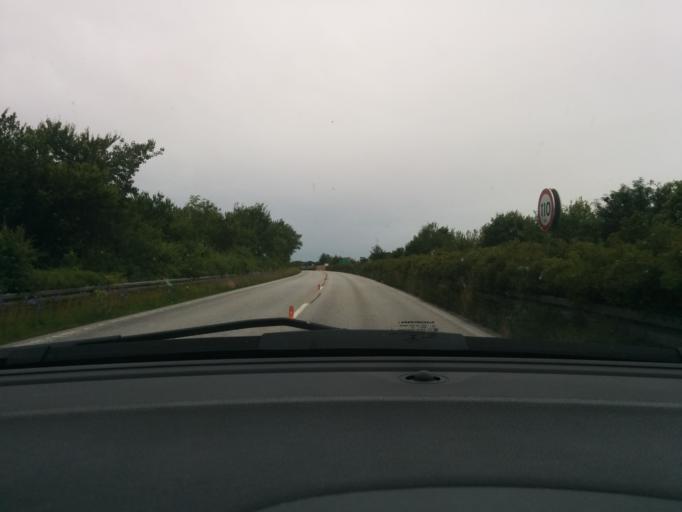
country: DK
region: Zealand
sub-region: Lolland Kommune
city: Maribo
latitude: 54.7775
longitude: 11.4760
